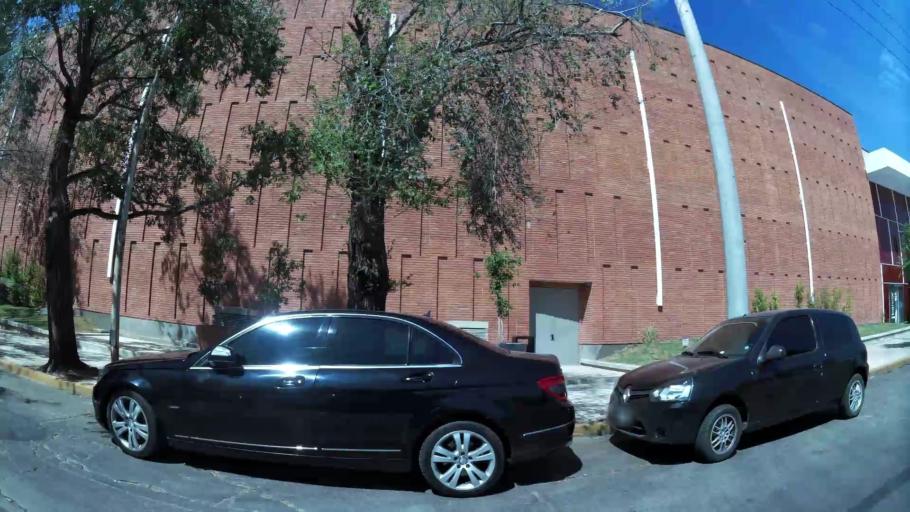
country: AR
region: Cordoba
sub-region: Departamento de Capital
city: Cordoba
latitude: -31.4118
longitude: -64.2420
